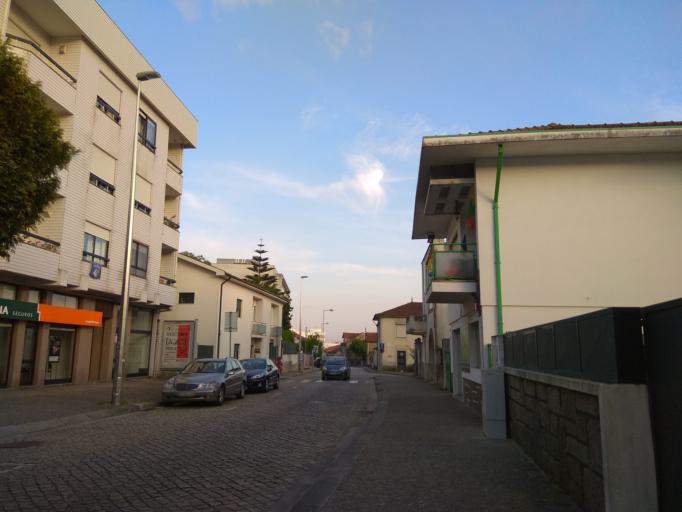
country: PT
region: Porto
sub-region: Maia
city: Maia
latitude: 41.2317
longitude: -8.6211
